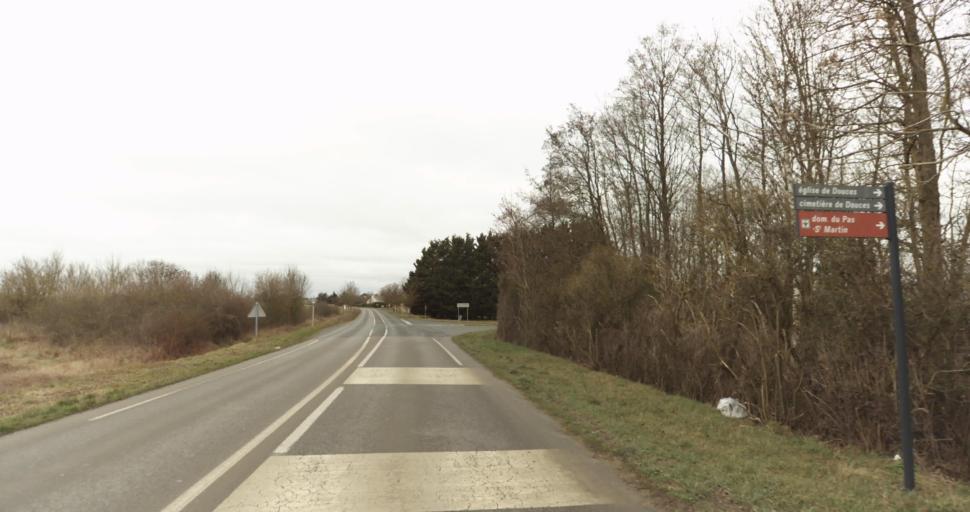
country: FR
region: Pays de la Loire
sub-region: Departement de Maine-et-Loire
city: Doue-la-Fontaine
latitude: 47.1826
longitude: -0.2640
